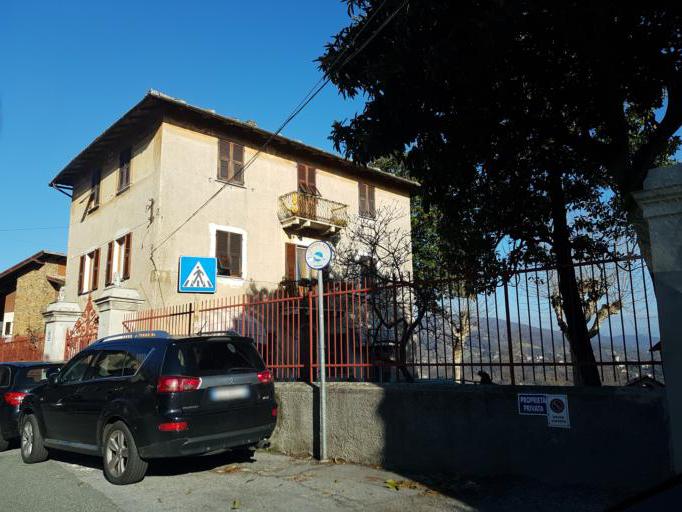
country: IT
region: Liguria
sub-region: Provincia di Genova
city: Campomorone
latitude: 44.5033
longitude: 8.8736
